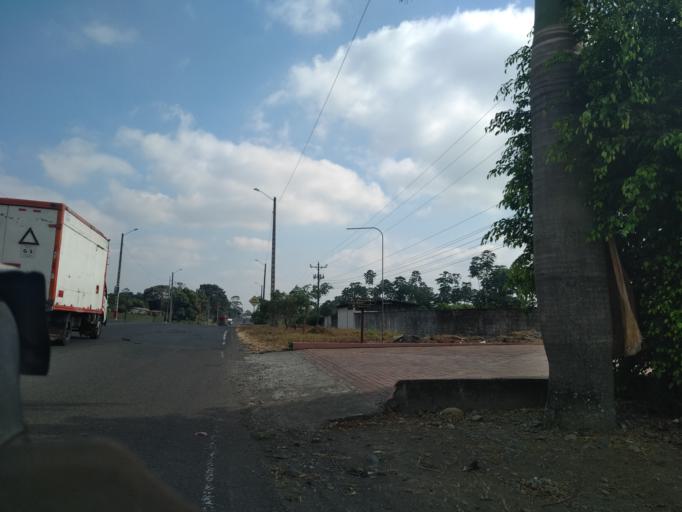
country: EC
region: Los Rios
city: Quevedo
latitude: -1.0709
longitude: -79.4965
